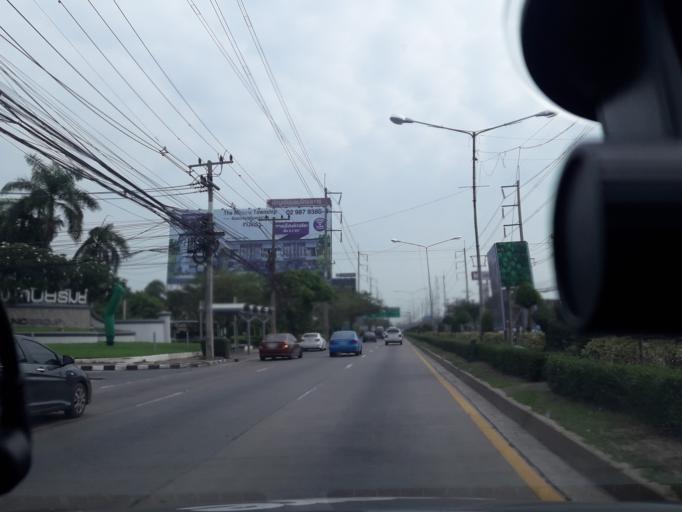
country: TH
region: Pathum Thani
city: Lam Luk Ka
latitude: 13.9347
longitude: 100.7397
